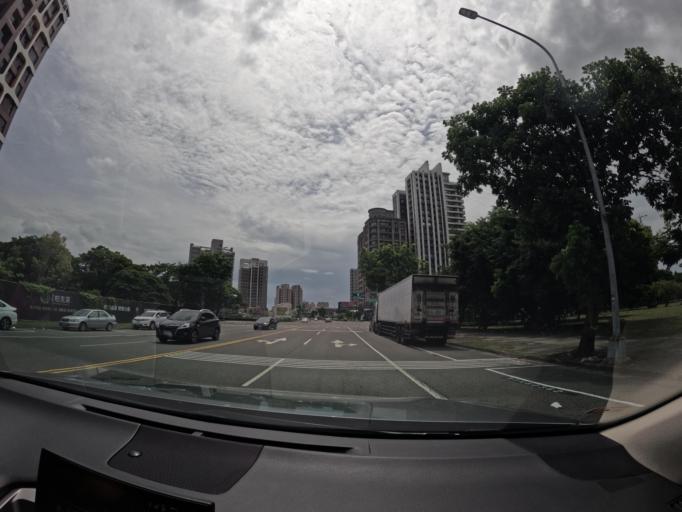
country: TW
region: Kaohsiung
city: Kaohsiung
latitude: 22.7283
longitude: 120.2856
